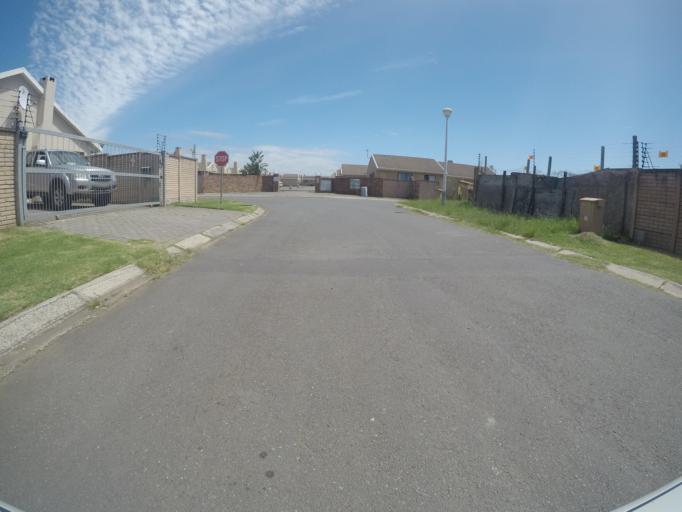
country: ZA
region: Eastern Cape
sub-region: Buffalo City Metropolitan Municipality
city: East London
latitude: -32.9485
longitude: 27.9990
